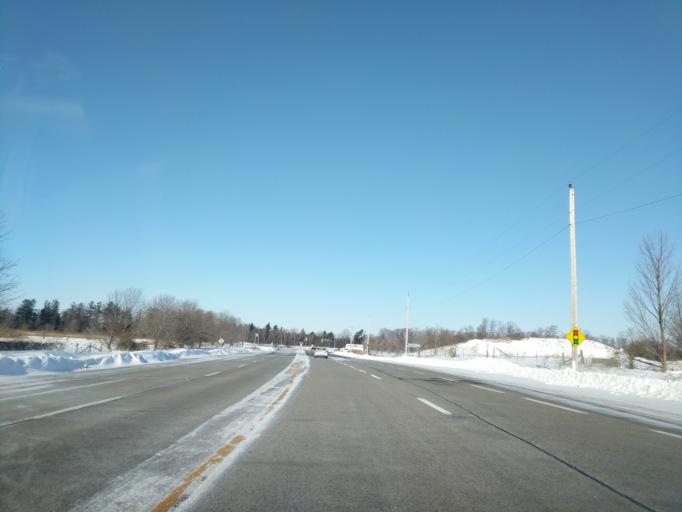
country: CA
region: Ontario
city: Pickering
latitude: 43.8683
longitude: -79.1381
